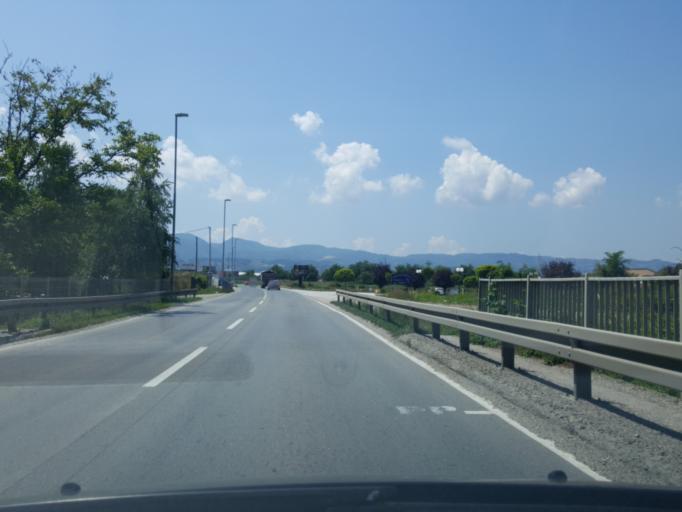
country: RS
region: Central Serbia
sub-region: Moravicki Okrug
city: Cacak
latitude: 43.8956
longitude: 20.3893
